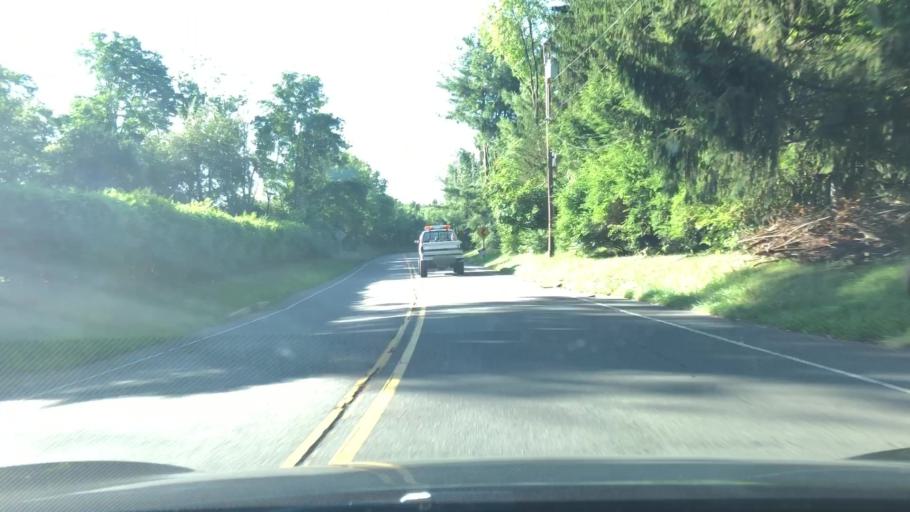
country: US
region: New Jersey
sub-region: Mercer County
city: Pennington
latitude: 40.3182
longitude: -74.8165
